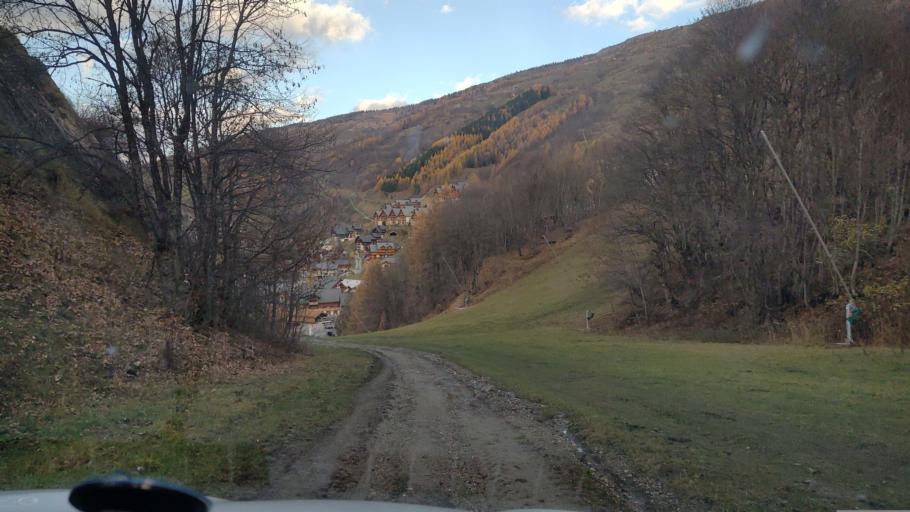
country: FR
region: Rhone-Alpes
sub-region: Departement de la Savoie
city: Valloire
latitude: 45.1604
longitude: 6.4277
